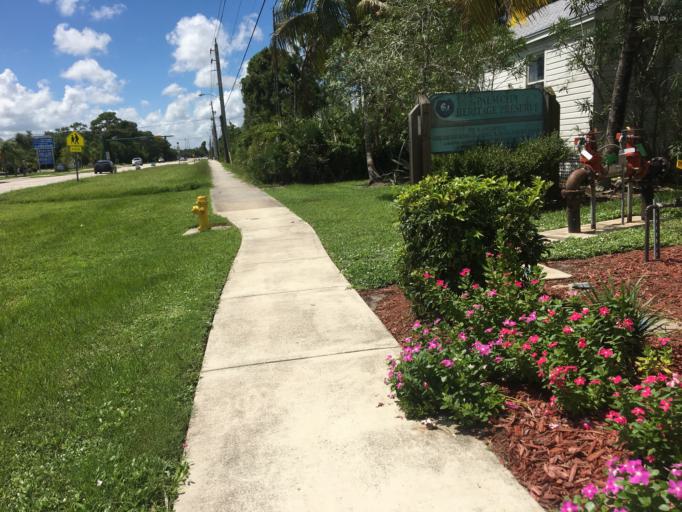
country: US
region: Florida
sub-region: Martin County
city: Palm City
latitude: 27.1667
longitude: -80.2695
